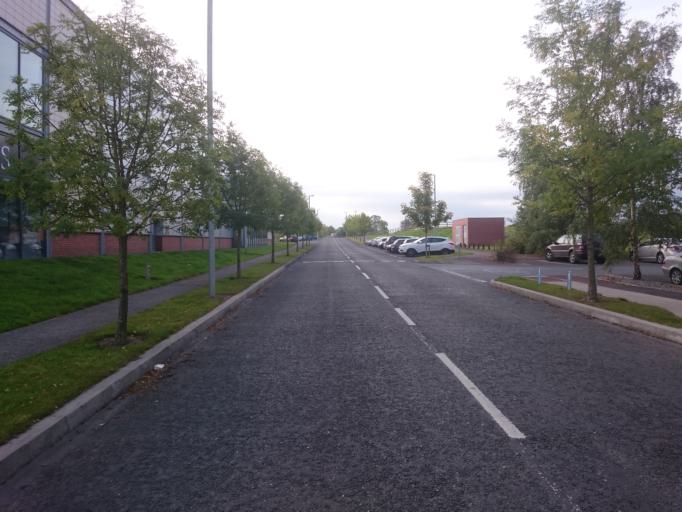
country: IE
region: Leinster
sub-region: Kilkenny
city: Kilkenny
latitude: 52.6347
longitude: -7.2481
